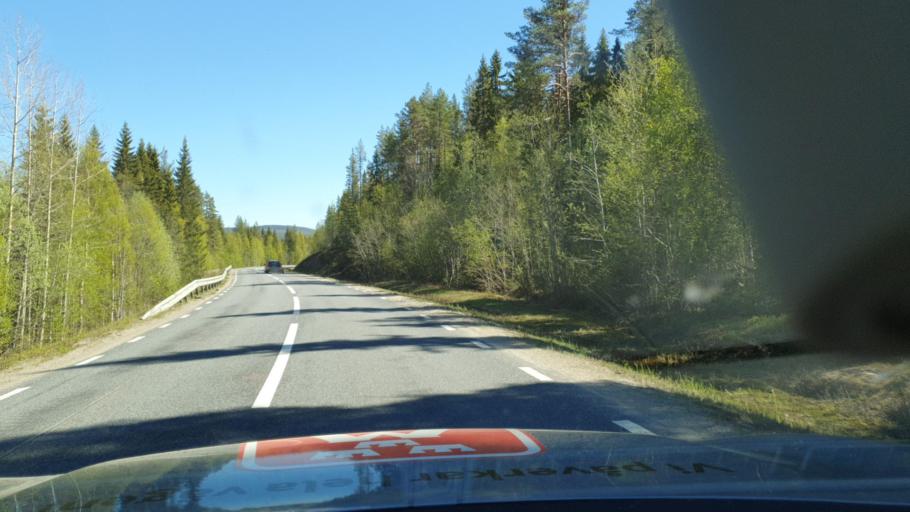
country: SE
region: Vaesternorrland
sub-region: OErnskoeldsviks Kommun
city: Bredbyn
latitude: 63.8055
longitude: 18.4850
